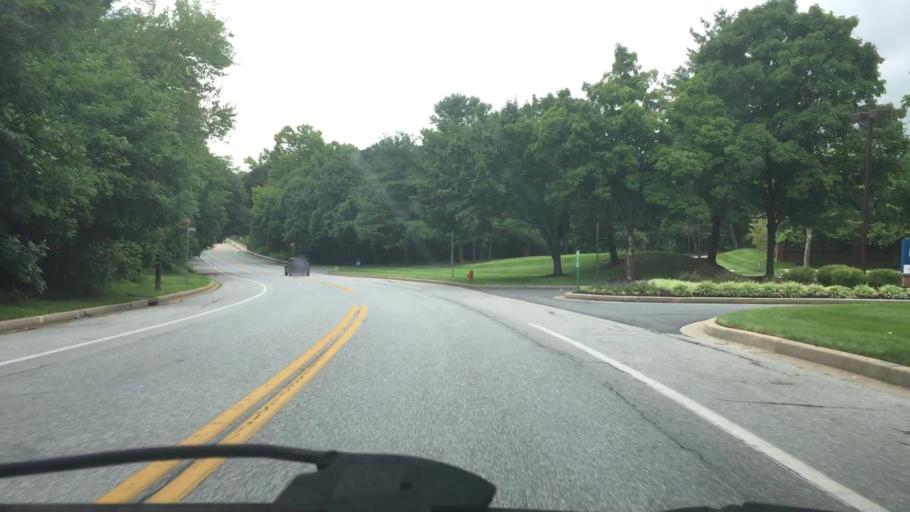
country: US
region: Maryland
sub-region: Howard County
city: Riverside
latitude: 39.1698
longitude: -76.8493
